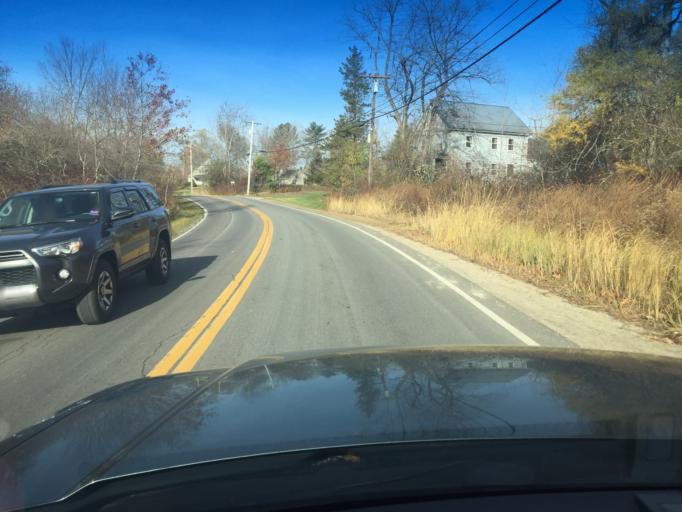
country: US
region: Maine
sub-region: York County
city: Eliot
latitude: 43.1775
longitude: -70.7258
